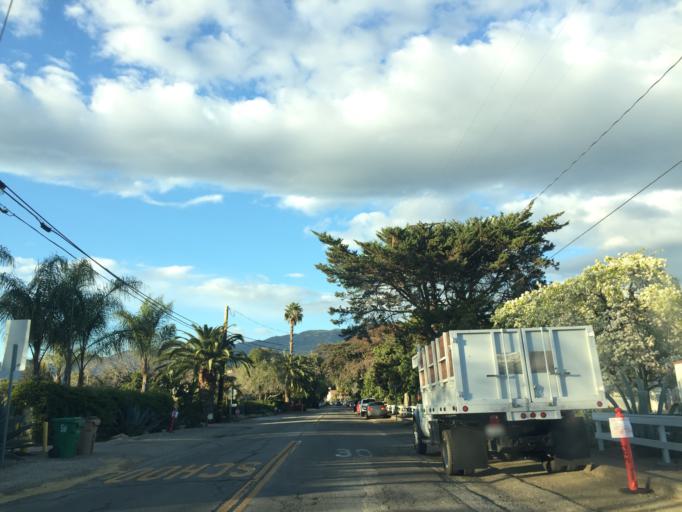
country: US
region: California
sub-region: Santa Barbara County
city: Goleta
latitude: 34.4369
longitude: -119.7711
